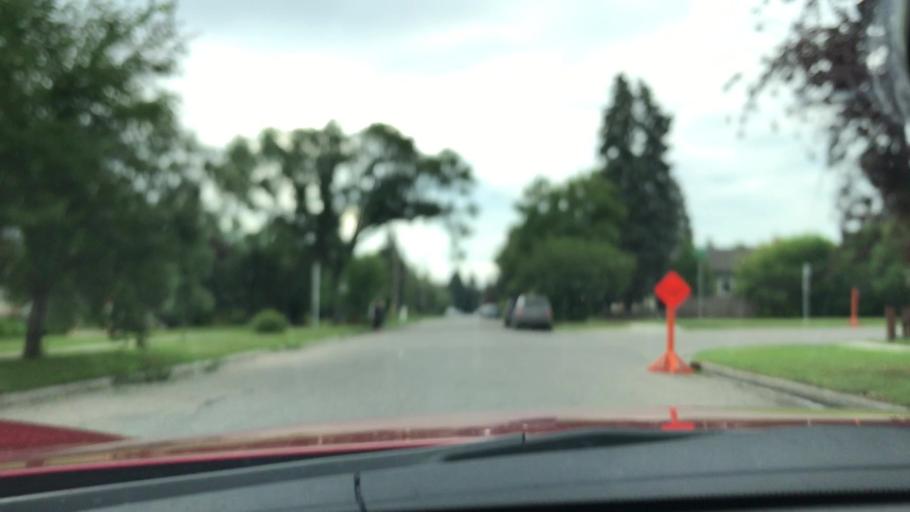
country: CA
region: Alberta
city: Calgary
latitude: 51.0402
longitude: -114.0287
